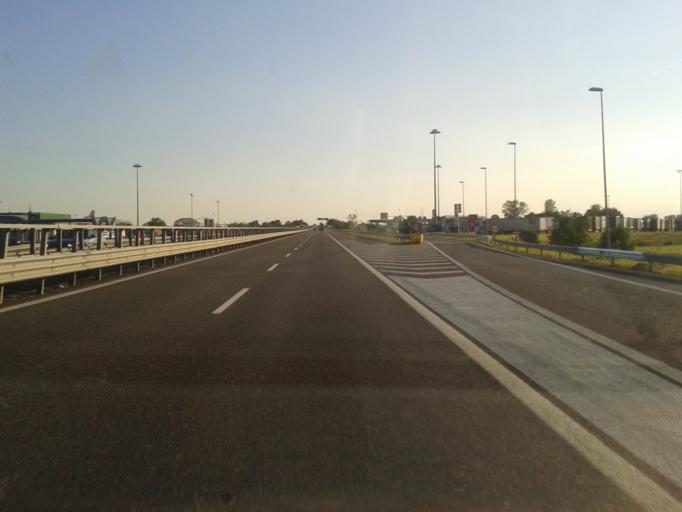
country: IT
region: Piedmont
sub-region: Provincia di Alessandria
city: Pozzolo Formigaro
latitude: 44.8023
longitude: 8.7526
